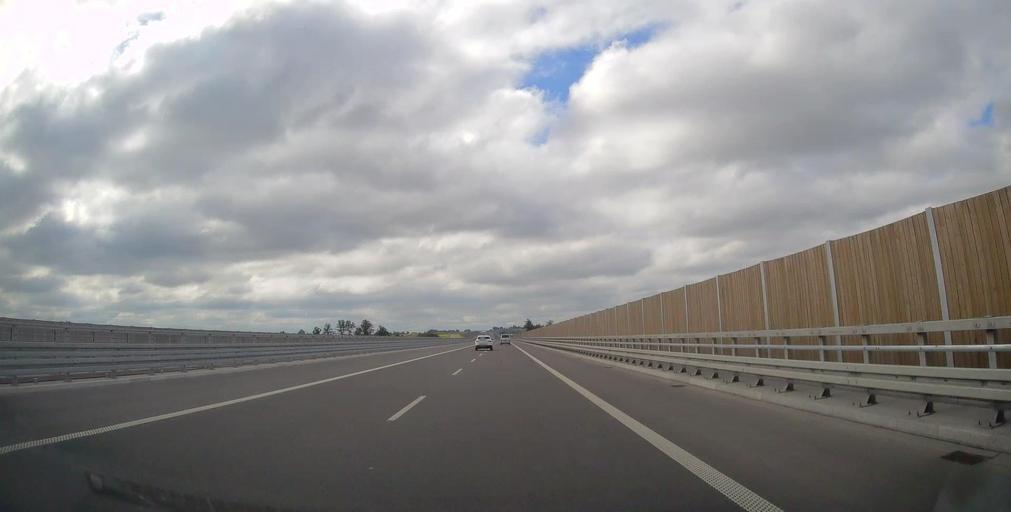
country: PL
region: Lesser Poland Voivodeship
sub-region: Powiat miechowski
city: Miechow
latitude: 50.2973
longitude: 20.0253
